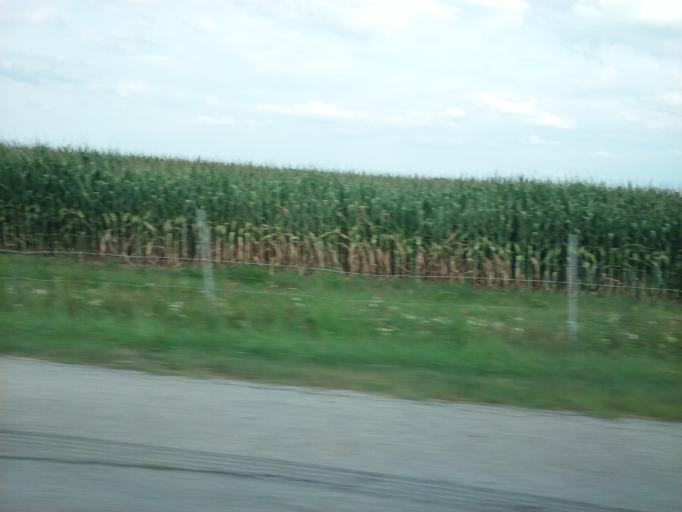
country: US
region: Ohio
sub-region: Wood County
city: Bowling Green
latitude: 41.3077
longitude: -83.6503
